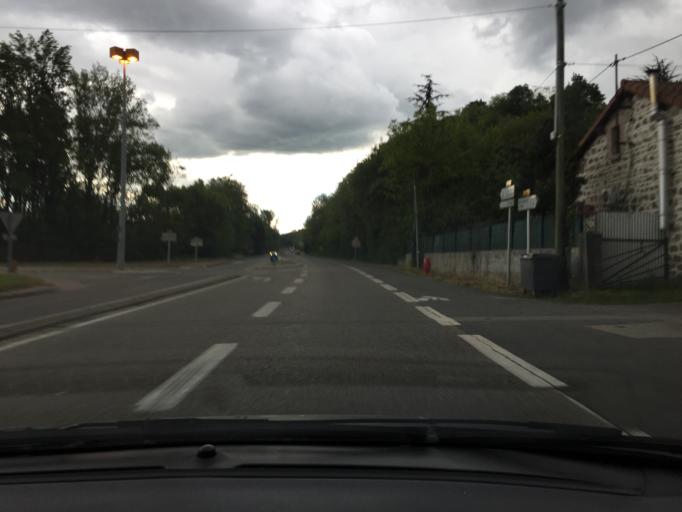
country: FR
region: Rhone-Alpes
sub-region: Departement du Rhone
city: Montagny
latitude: 45.6299
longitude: 4.7578
